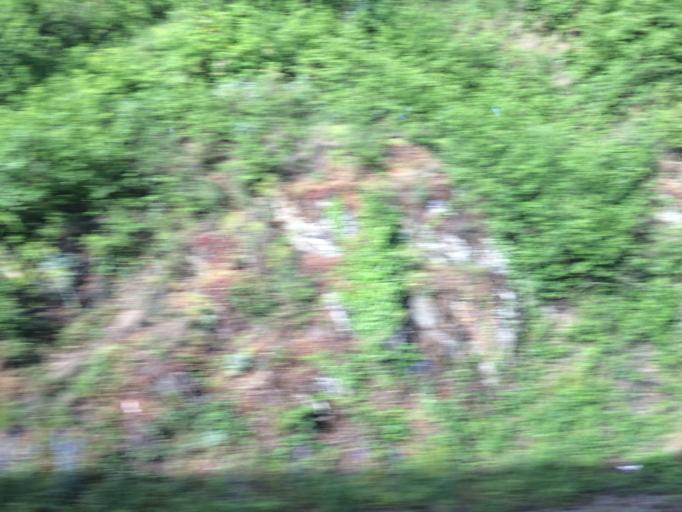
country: DE
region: Rheinland-Pfalz
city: Filsen
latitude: 50.2364
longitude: 7.5850
